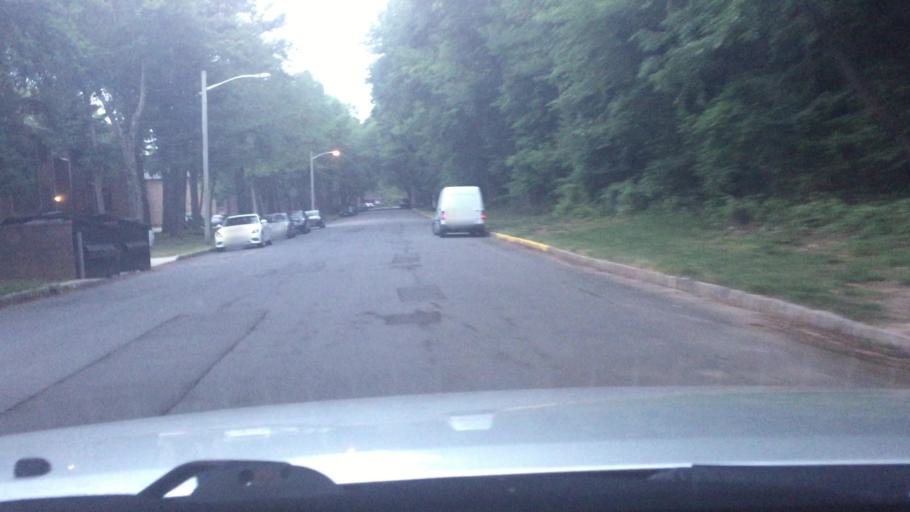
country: US
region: New Jersey
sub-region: Middlesex County
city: Kendall Park
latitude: 40.4380
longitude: -74.5204
